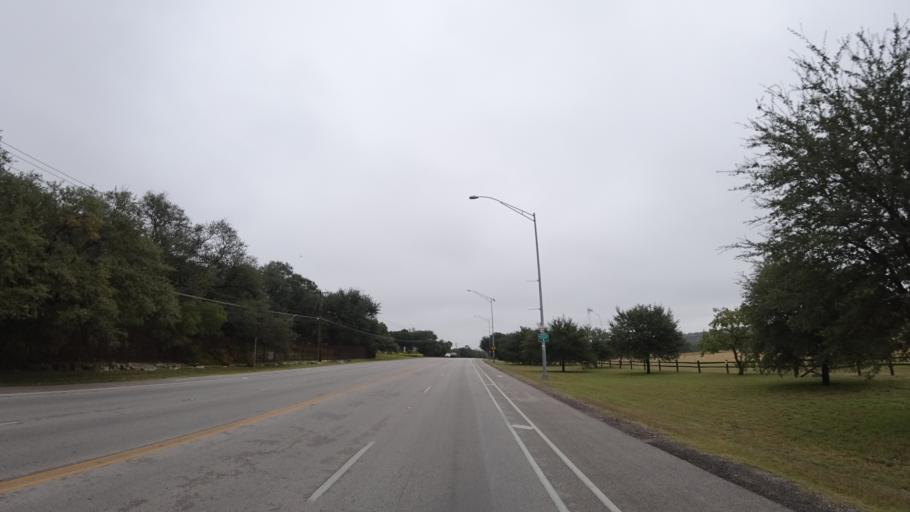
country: US
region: Texas
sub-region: Travis County
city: Rollingwood
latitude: 30.2686
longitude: -97.7737
